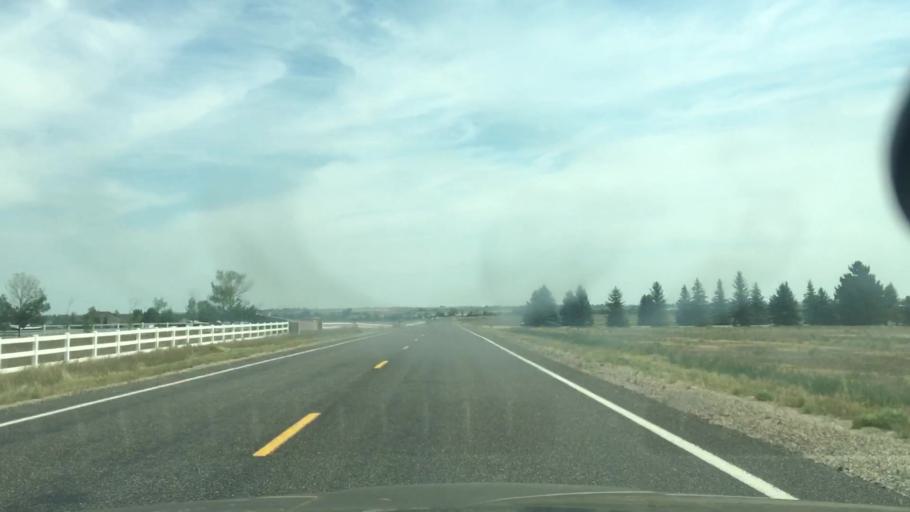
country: US
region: Colorado
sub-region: Larimer County
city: Berthoud
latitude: 40.3349
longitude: -105.1586
